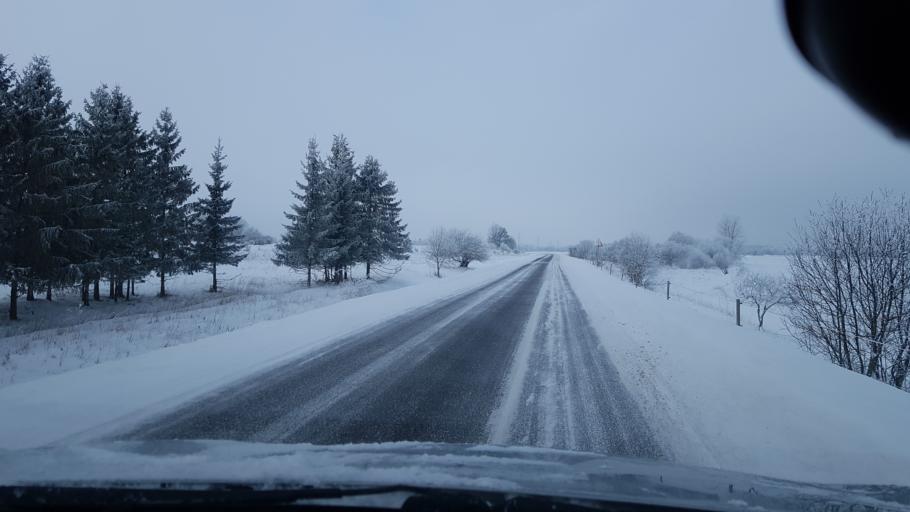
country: EE
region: Harju
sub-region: Keila linn
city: Keila
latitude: 59.3376
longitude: 24.4542
